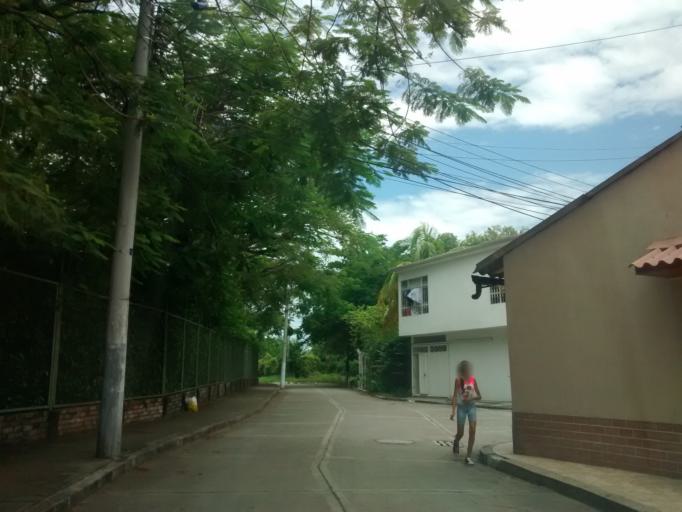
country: CO
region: Cundinamarca
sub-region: Girardot
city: Girardot City
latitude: 4.3085
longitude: -74.8099
